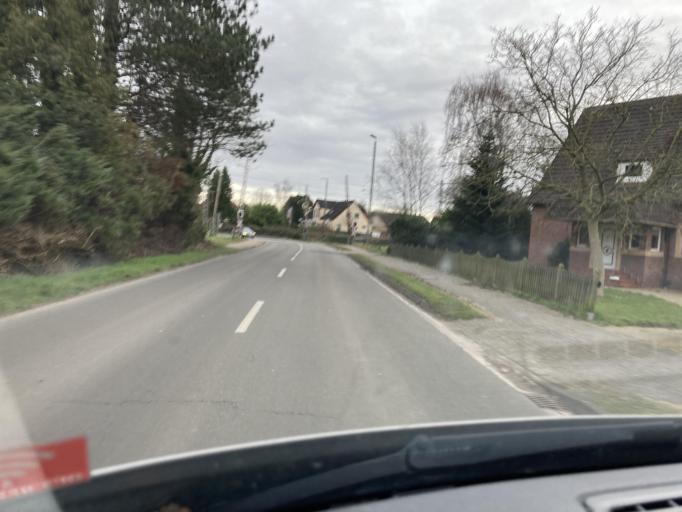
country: DE
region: Lower Saxony
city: Leer
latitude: 53.1661
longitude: 7.4471
